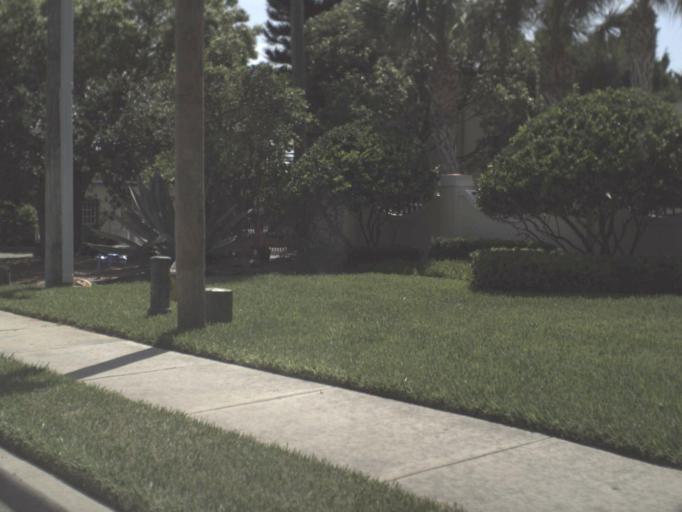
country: US
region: Florida
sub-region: Pinellas County
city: Clearwater
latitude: 27.9888
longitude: -82.7958
